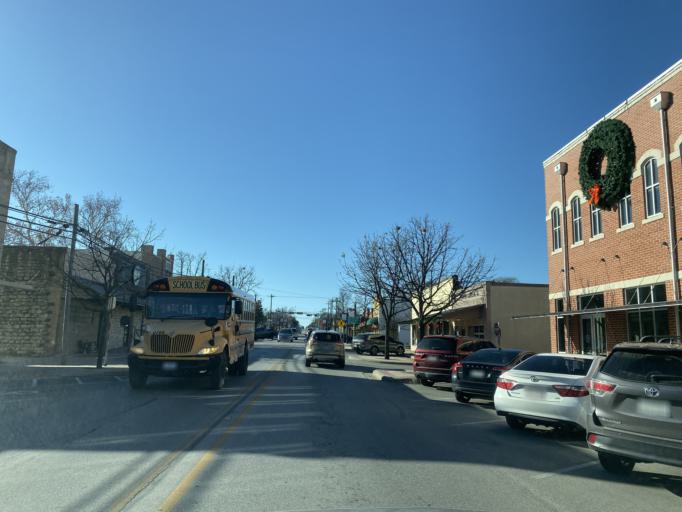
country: US
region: Texas
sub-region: Hays County
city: Kyle
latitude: 29.9885
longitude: -97.8756
